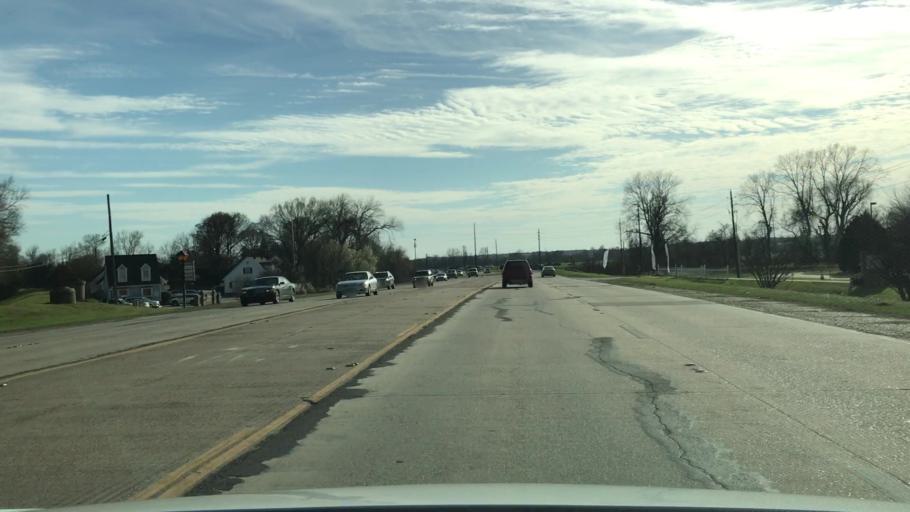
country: US
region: Louisiana
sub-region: Bossier Parish
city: Bossier City
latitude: 32.4424
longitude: -93.7041
